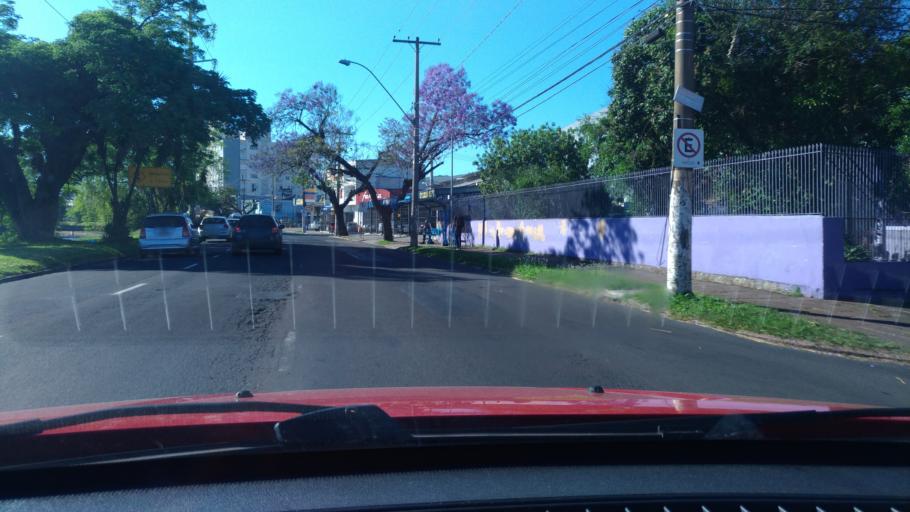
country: BR
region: Rio Grande do Sul
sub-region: Porto Alegre
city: Porto Alegre
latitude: -30.0528
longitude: -51.1938
